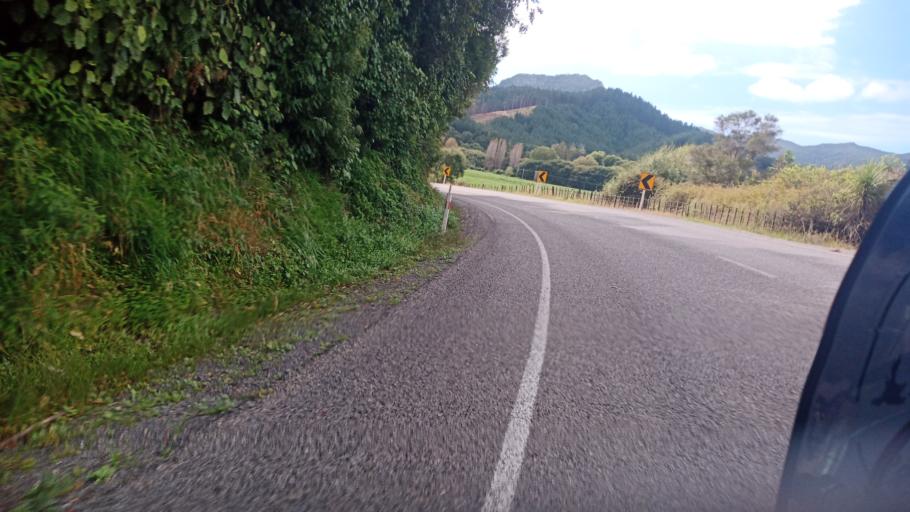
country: NZ
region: Gisborne
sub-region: Gisborne District
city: Gisborne
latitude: -38.2228
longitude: 178.2585
